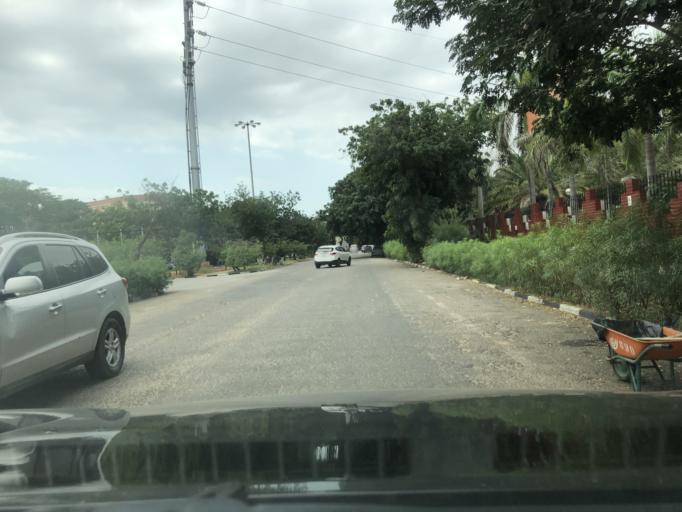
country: AO
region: Luanda
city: Luanda
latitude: -8.8292
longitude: 13.2406
